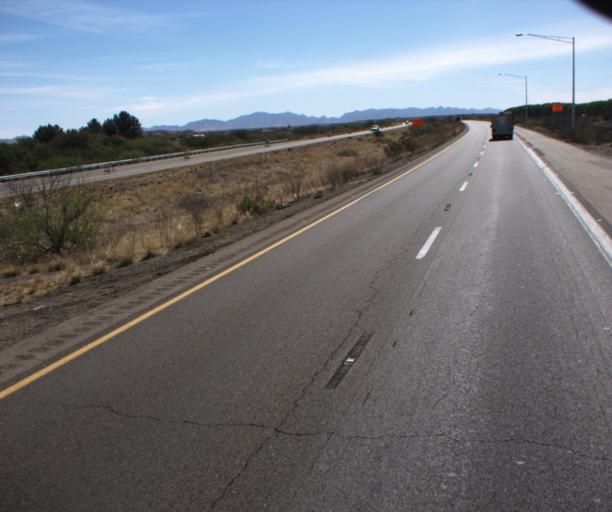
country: US
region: Arizona
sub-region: Cochise County
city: Benson
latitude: 31.9675
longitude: -110.2773
